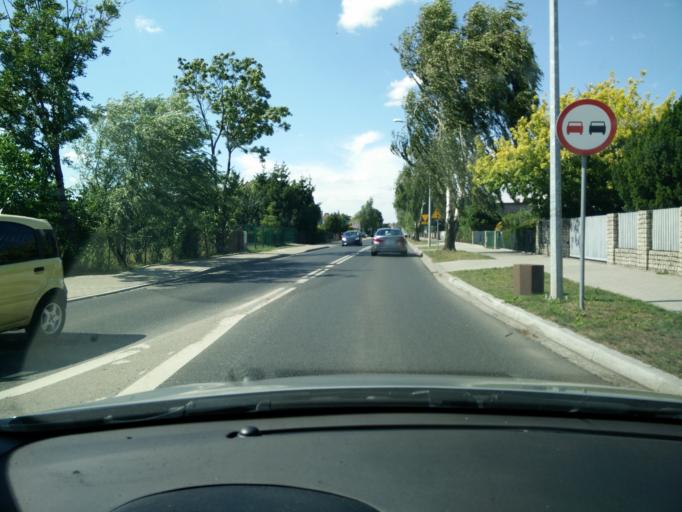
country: PL
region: Greater Poland Voivodeship
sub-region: Powiat sredzki
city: Sroda Wielkopolska
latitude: 52.2221
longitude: 17.2867
